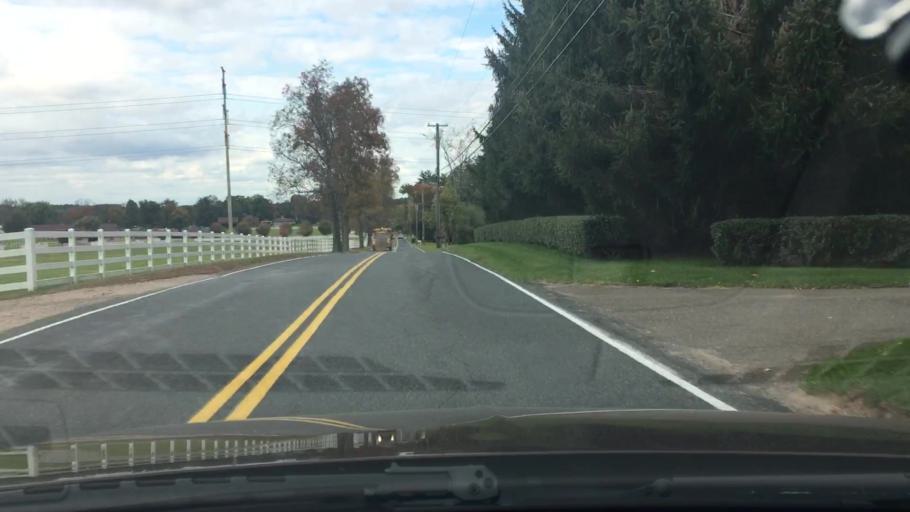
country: US
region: Connecticut
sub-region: Tolland County
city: Somers
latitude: 41.9740
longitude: -72.4839
